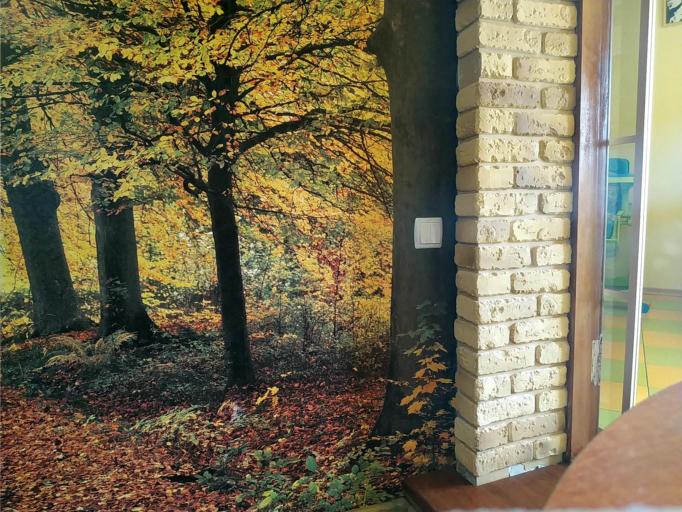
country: RU
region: Smolensk
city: Katyn'
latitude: 54.9563
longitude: 31.7189
